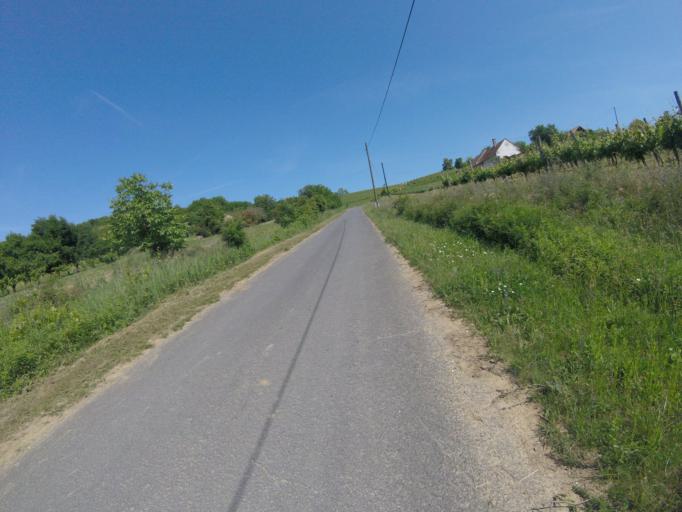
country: HU
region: Zala
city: Zalaszentgrot
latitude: 46.9227
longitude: 17.0533
